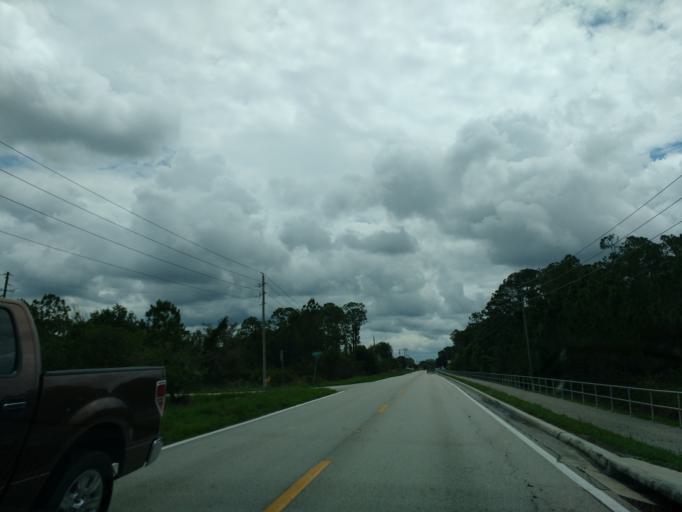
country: US
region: Florida
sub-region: Highlands County
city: Sebring
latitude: 27.4709
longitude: -81.4897
